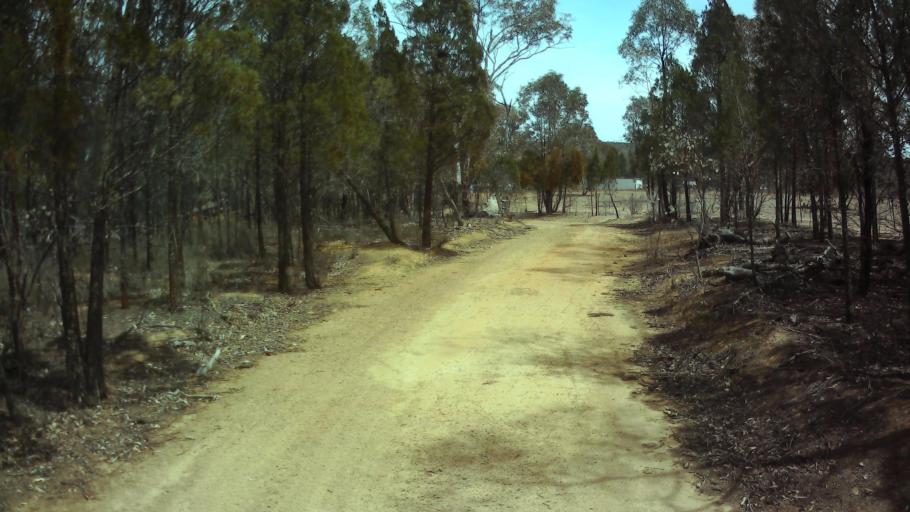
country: AU
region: New South Wales
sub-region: Weddin
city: Grenfell
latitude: -33.8848
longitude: 148.3813
